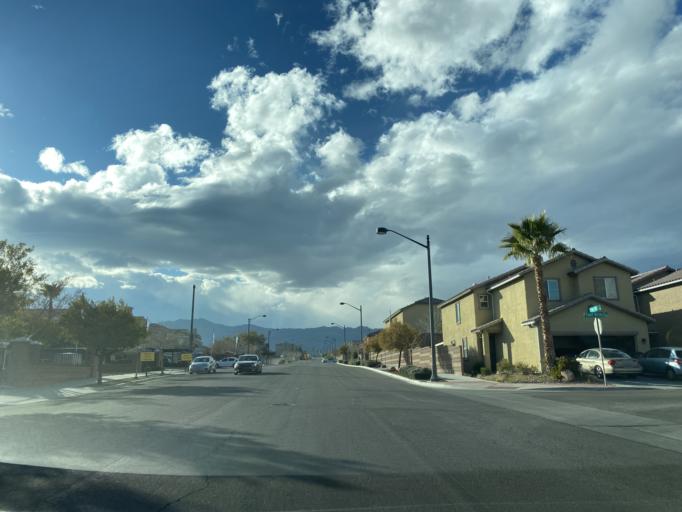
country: US
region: Nevada
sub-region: Clark County
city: Summerlin South
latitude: 36.2828
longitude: -115.2951
